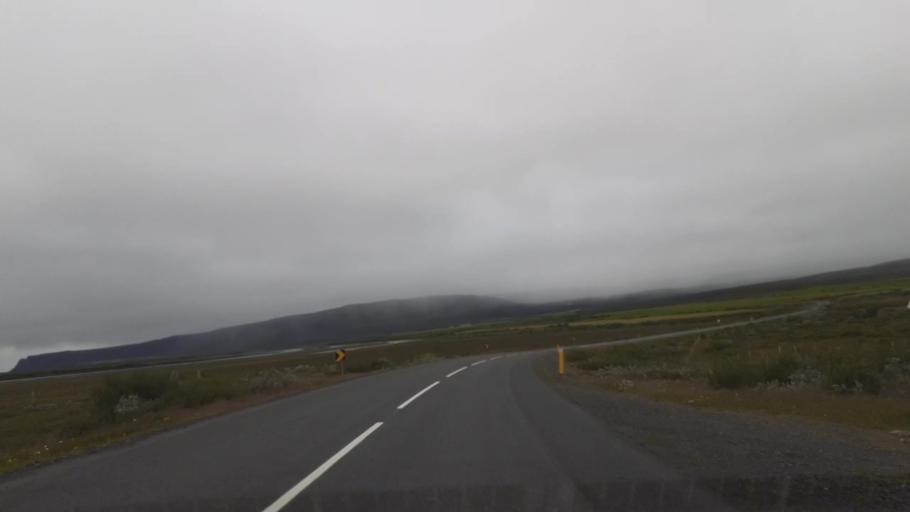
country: IS
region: Northeast
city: Husavik
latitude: 66.1074
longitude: -16.4443
